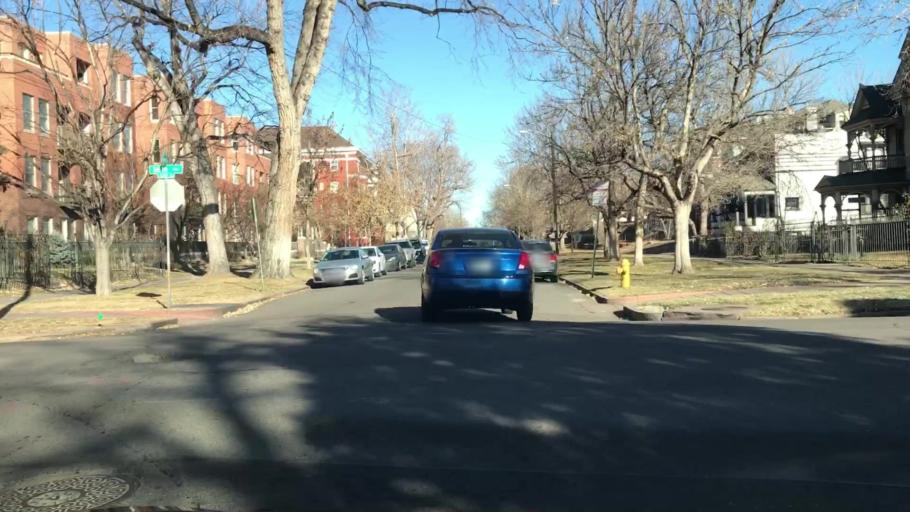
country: US
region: Colorado
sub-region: Denver County
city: Denver
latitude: 39.7416
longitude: -104.9762
